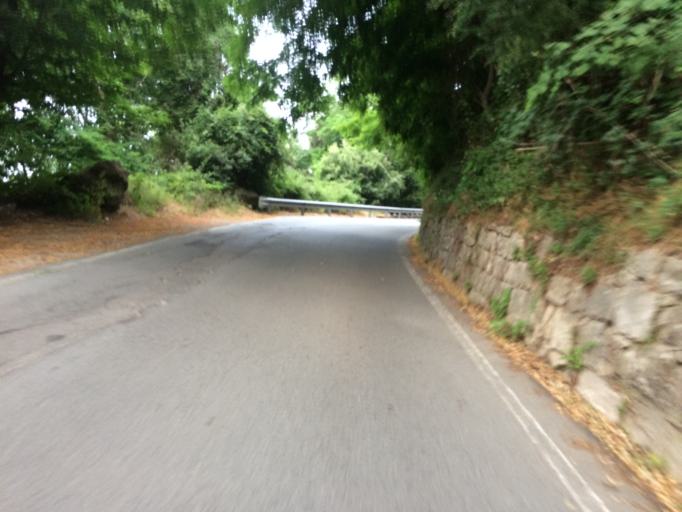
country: IT
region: Liguria
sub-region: Provincia di Imperia
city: Seborga
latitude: 43.8521
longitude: 7.7334
